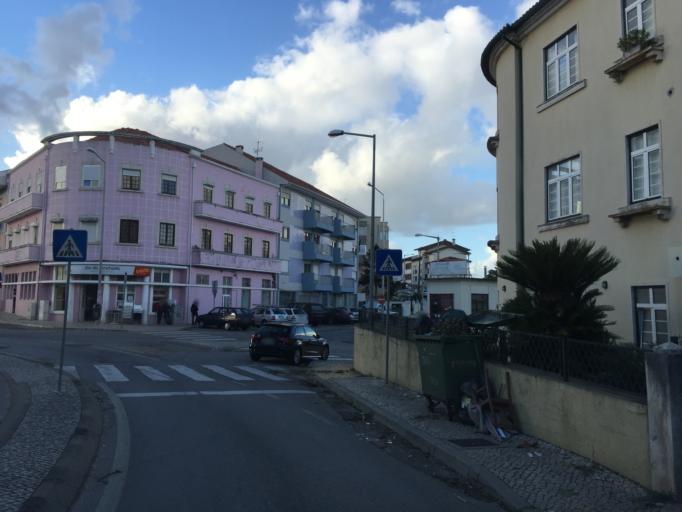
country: PT
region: Coimbra
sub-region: Coimbra
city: Coimbra
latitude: 40.2145
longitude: -8.4283
